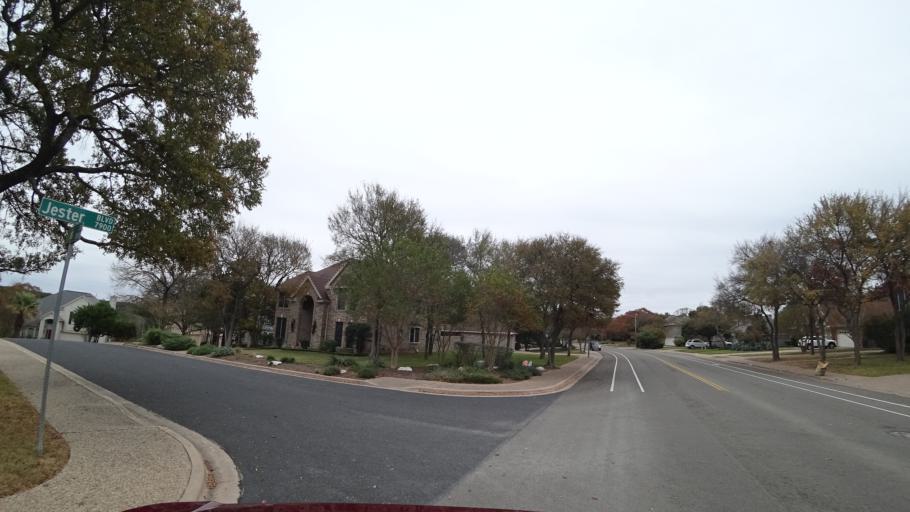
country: US
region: Texas
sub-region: Williamson County
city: Jollyville
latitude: 30.3898
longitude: -97.8016
